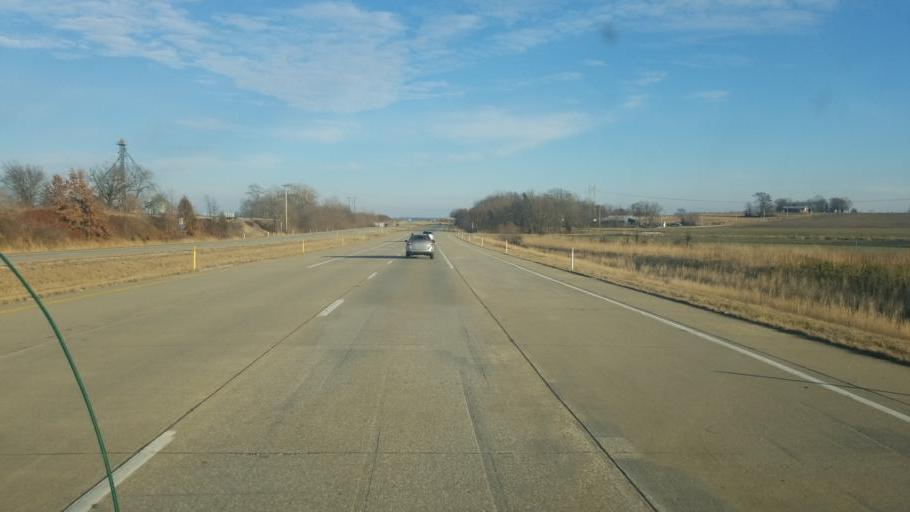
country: US
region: Indiana
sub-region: Knox County
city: Vincennes
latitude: 38.6795
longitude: -87.4053
